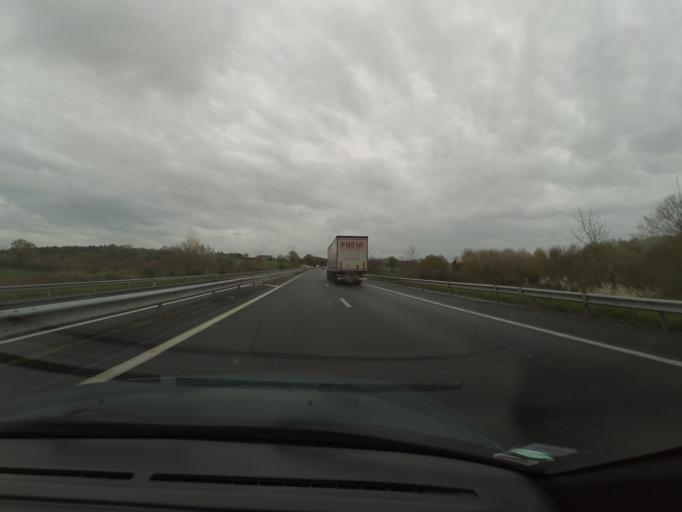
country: FR
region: Pays de la Loire
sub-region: Departement de Maine-et-Loire
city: Durtal
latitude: 47.6569
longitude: -0.2720
